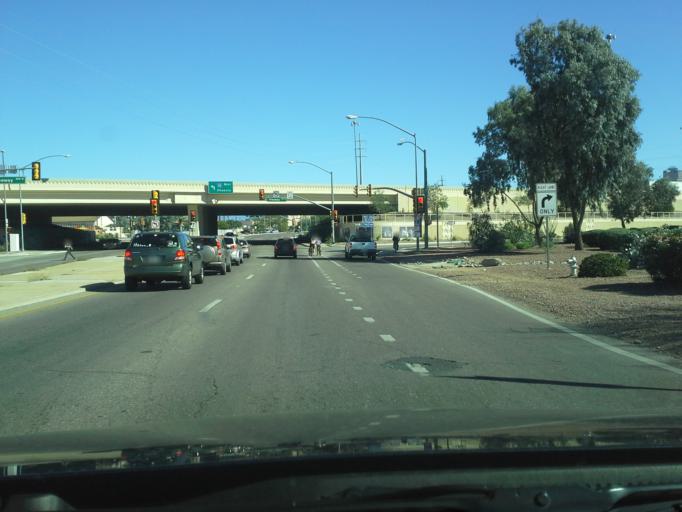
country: US
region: Arizona
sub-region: Pima County
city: South Tucson
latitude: 32.2294
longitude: -110.9836
